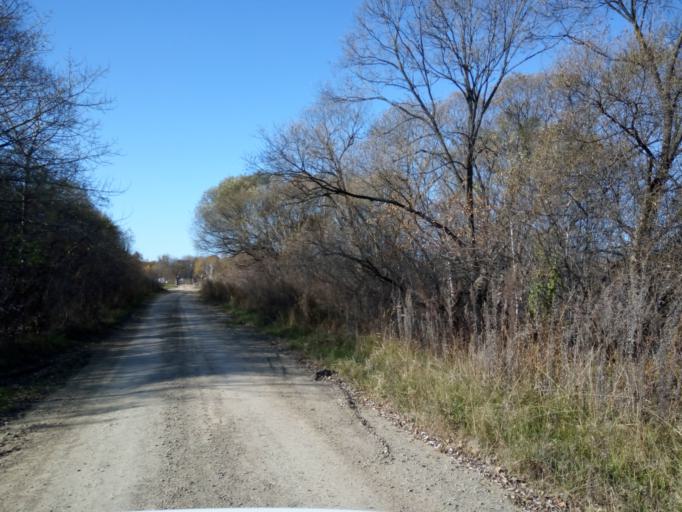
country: RU
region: Primorskiy
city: Dal'nerechensk
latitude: 45.9401
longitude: 133.6773
